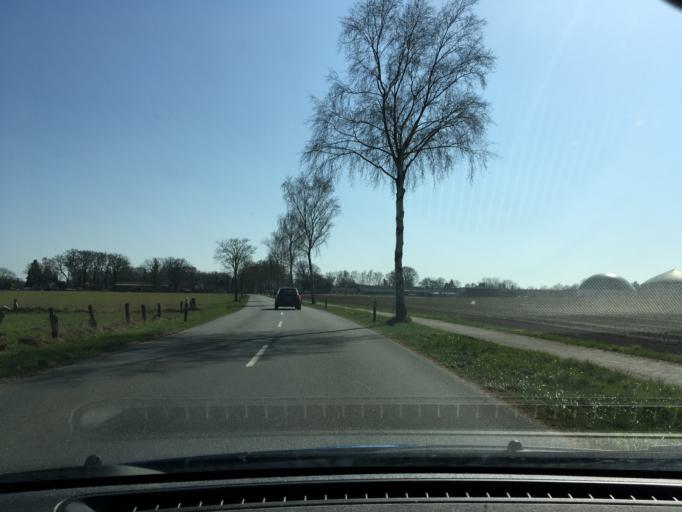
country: DE
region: Lower Saxony
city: Eimke
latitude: 52.9707
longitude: 10.3127
